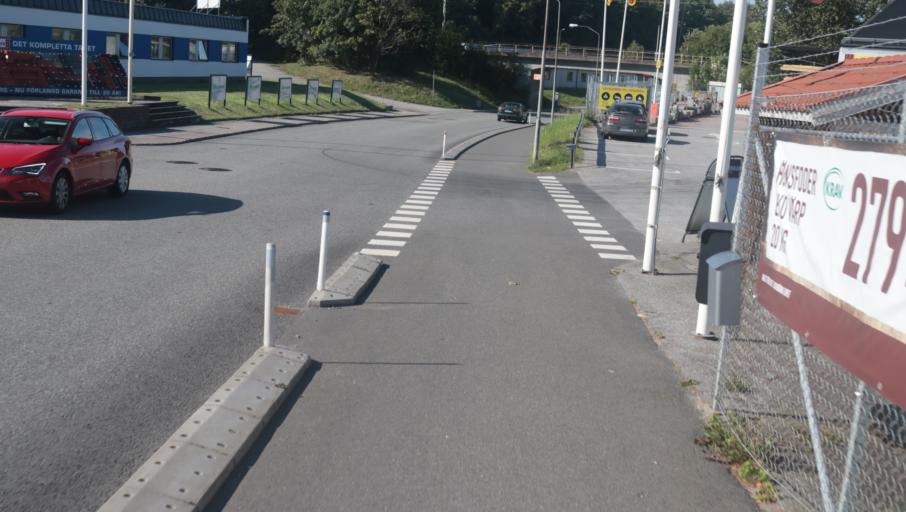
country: SE
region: Blekinge
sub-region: Karlshamns Kommun
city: Karlshamn
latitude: 56.1782
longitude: 14.8483
